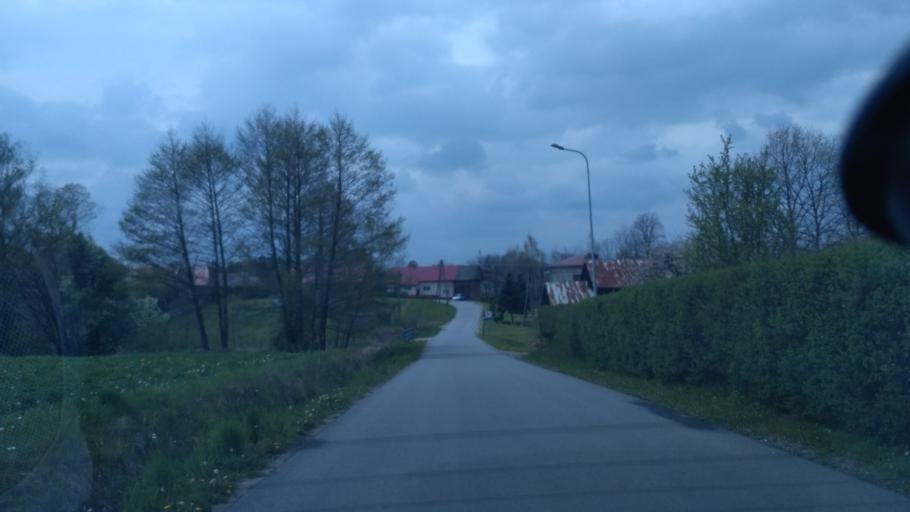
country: PL
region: Subcarpathian Voivodeship
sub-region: Powiat brzozowski
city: Haczow
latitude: 49.6748
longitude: 21.8951
